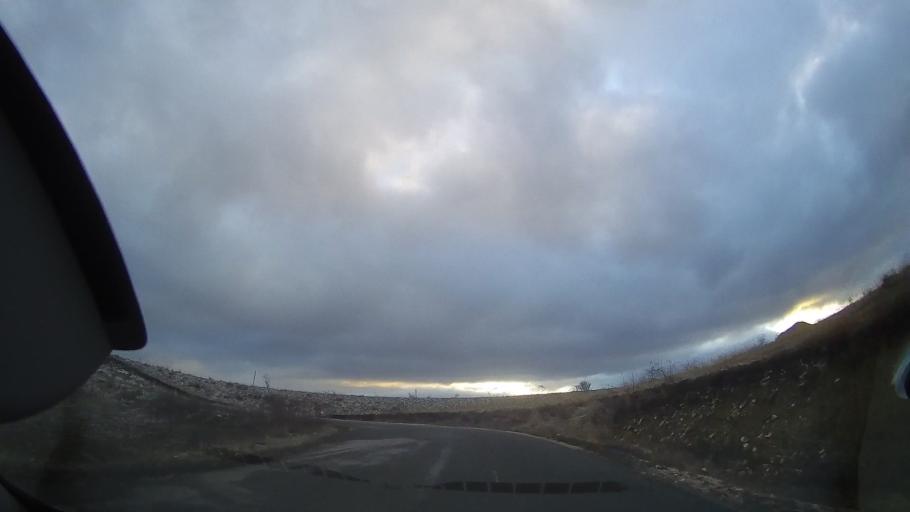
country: RO
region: Cluj
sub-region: Comuna Manastireni
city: Manastireni
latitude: 46.7795
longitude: 23.0548
